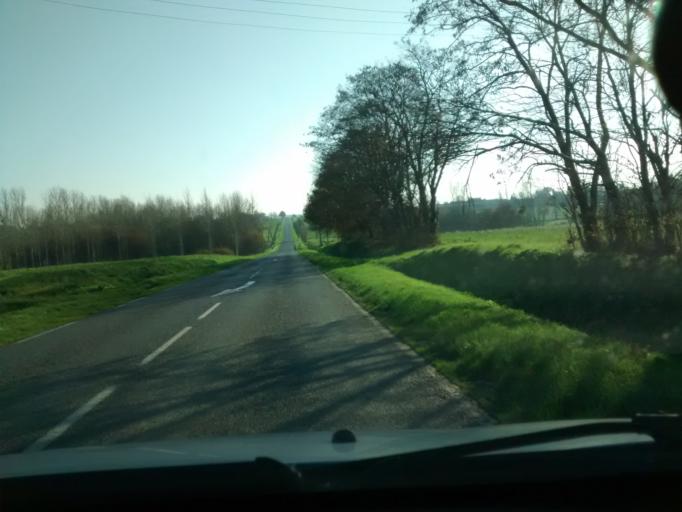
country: FR
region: Lower Normandy
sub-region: Departement de la Manche
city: Pontorson
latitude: 48.5166
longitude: -1.4802
